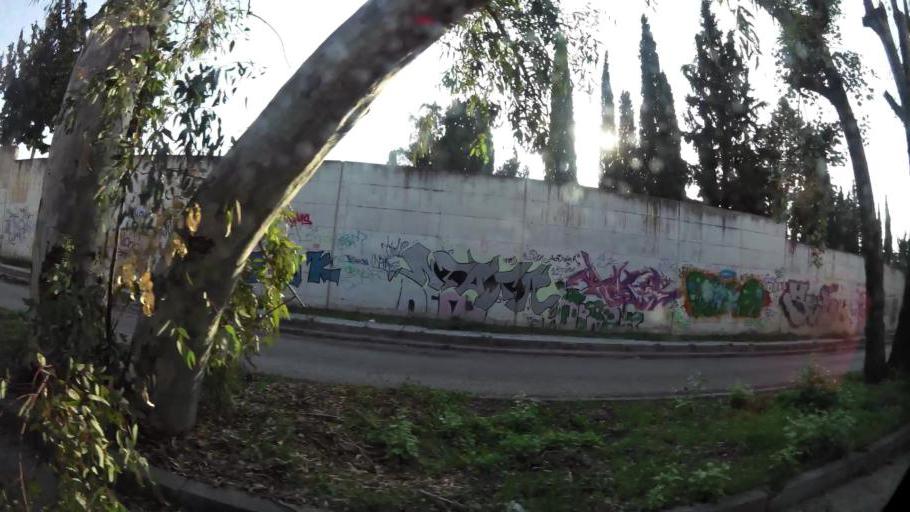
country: GR
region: Attica
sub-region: Nomarchia Athinas
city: Nea Filadelfeia
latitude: 38.0499
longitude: 23.7347
